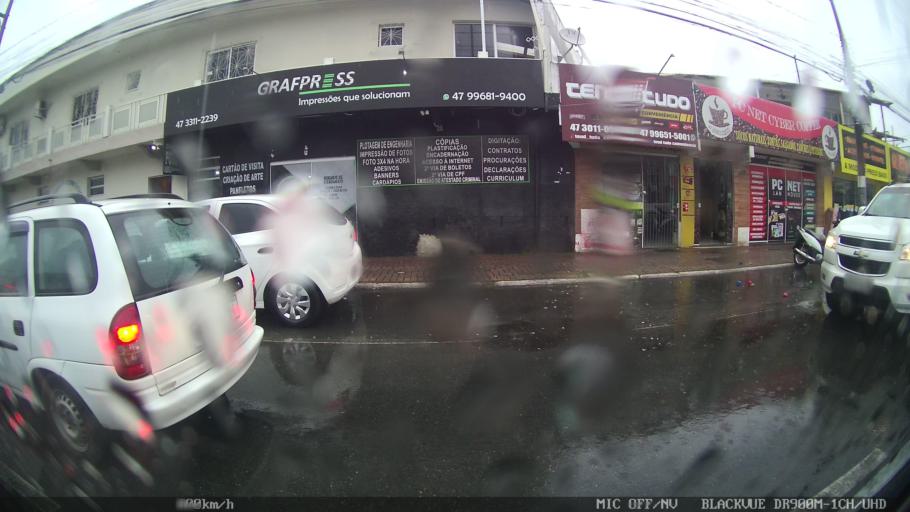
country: BR
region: Santa Catarina
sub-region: Balneario Camboriu
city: Balneario Camboriu
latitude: -27.0045
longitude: -48.6387
